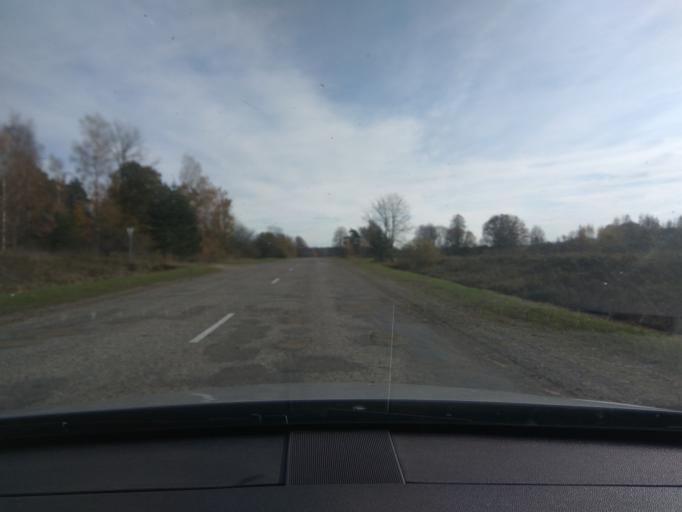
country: LV
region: Alsunga
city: Alsunga
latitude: 57.0000
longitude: 21.7497
